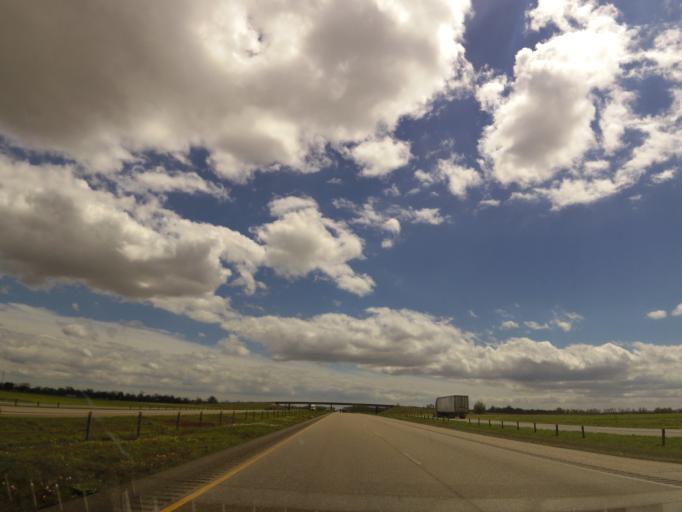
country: US
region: Arkansas
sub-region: Crittenden County
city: Marion
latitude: 35.2959
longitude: -90.2457
